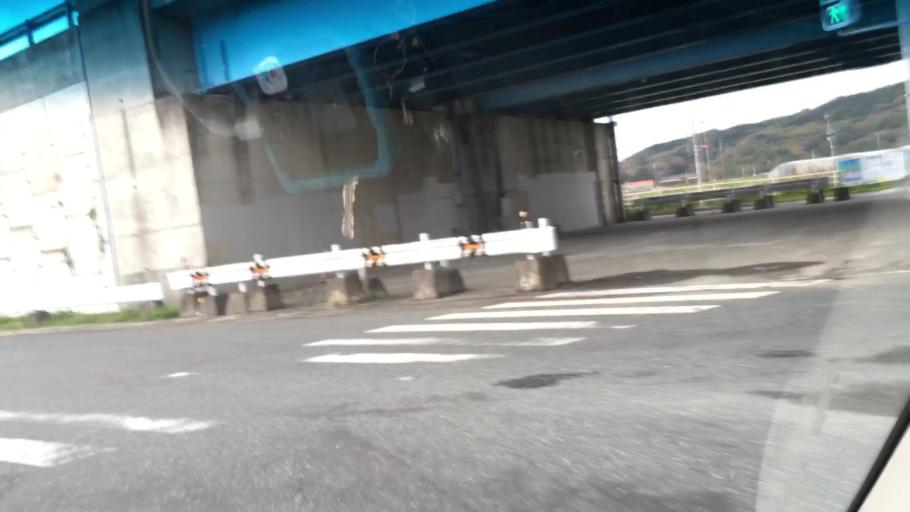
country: JP
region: Fukuoka
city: Maebaru-chuo
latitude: 33.5314
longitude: 130.1878
